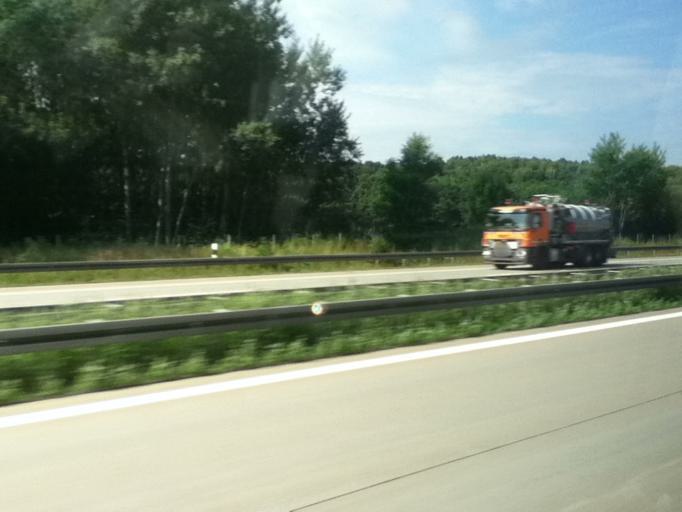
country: DE
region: Saxony
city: Wittgensdorf
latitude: 50.8499
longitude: 12.8259
